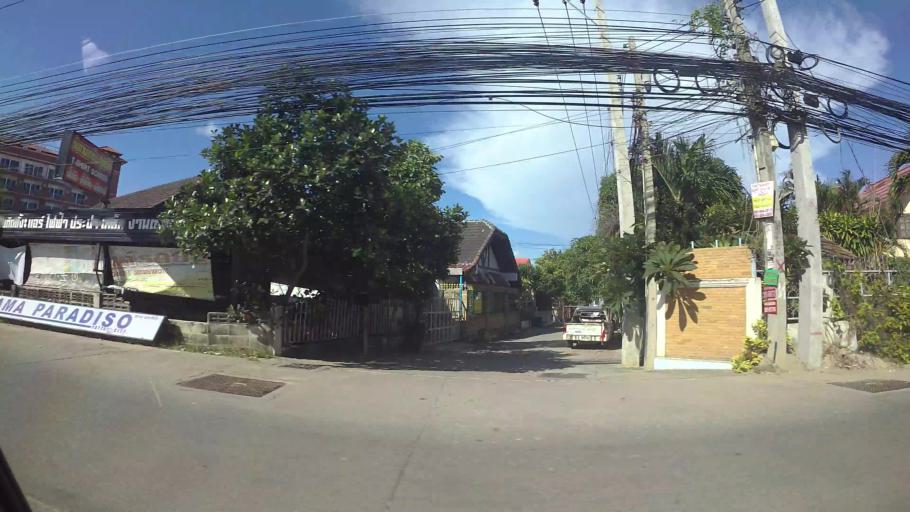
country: TH
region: Chon Buri
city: Phatthaya
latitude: 12.9093
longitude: 100.8811
